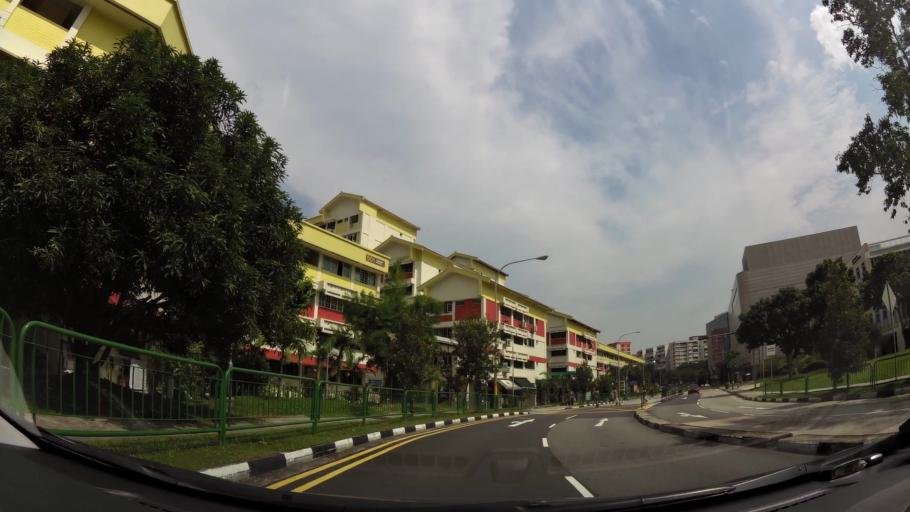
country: SG
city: Singapore
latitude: 1.3556
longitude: 103.9443
